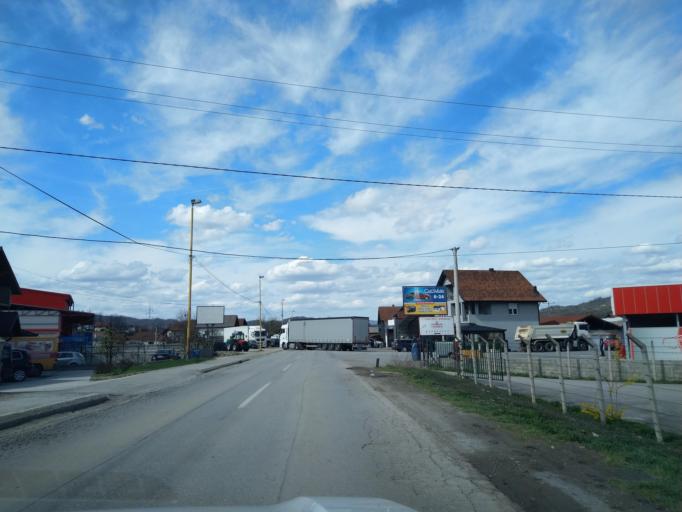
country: RS
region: Central Serbia
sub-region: Zlatiborski Okrug
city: Arilje
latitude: 43.7363
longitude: 20.1093
